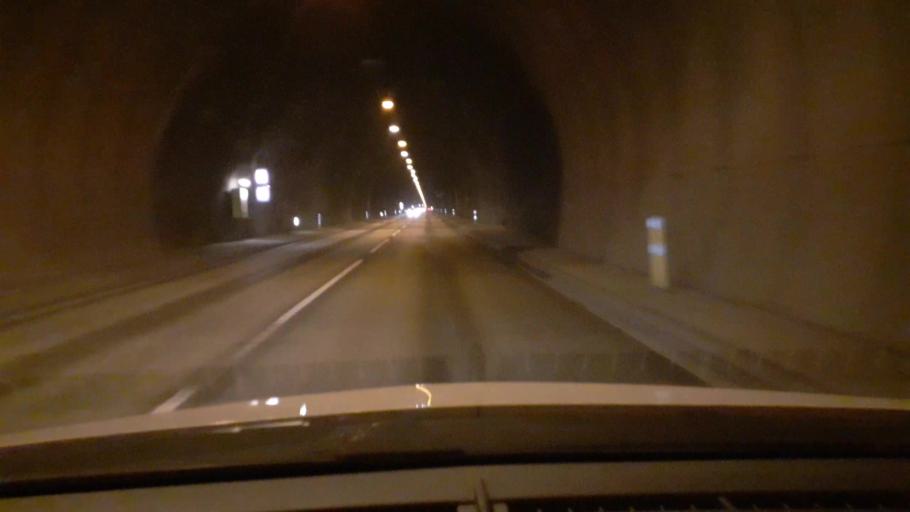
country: IS
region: Capital Region
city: Reykjavik
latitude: 64.2938
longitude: -21.8667
